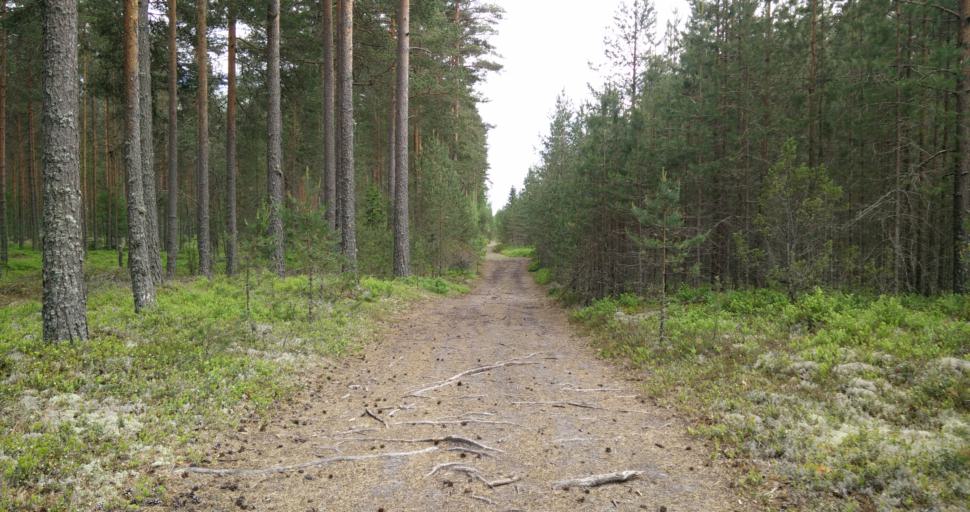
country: SE
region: Vaermland
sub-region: Hagfors Kommun
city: Hagfors
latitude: 60.0142
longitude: 13.5865
